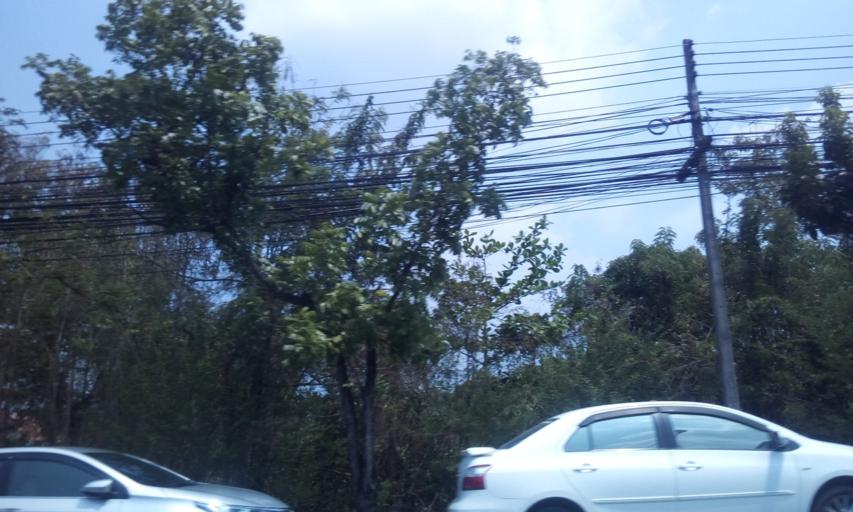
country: TH
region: Chachoengsao
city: Chachoengsao
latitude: 13.6729
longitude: 101.0843
